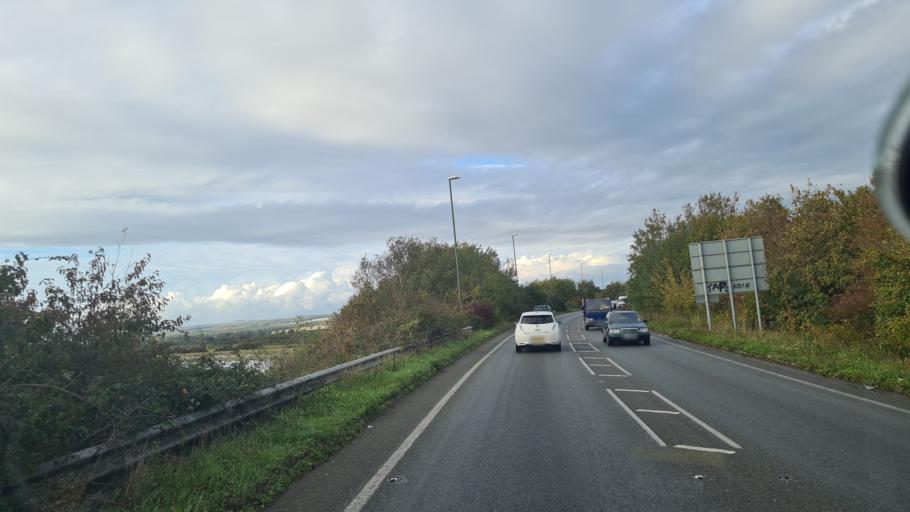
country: GB
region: England
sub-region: West Sussex
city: Littlehampton
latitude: 50.8161
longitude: -0.5596
